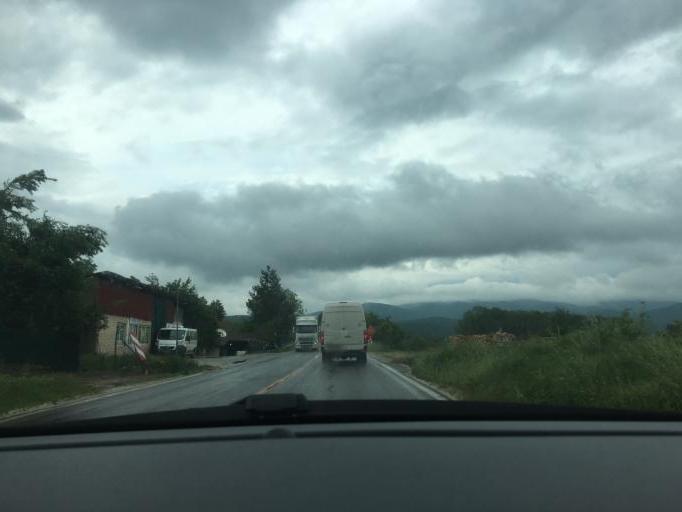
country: MK
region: Debarca
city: Belcista
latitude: 41.3293
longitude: 20.7986
